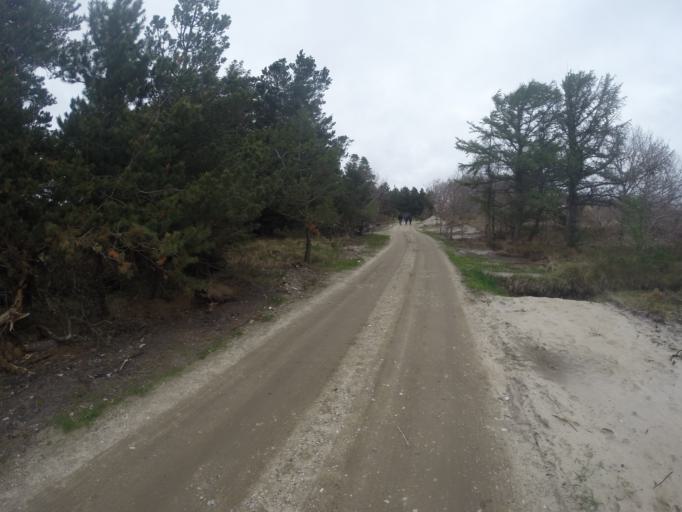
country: DK
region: North Denmark
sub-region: Thisted Kommune
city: Hurup
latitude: 56.8739
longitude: 8.3091
